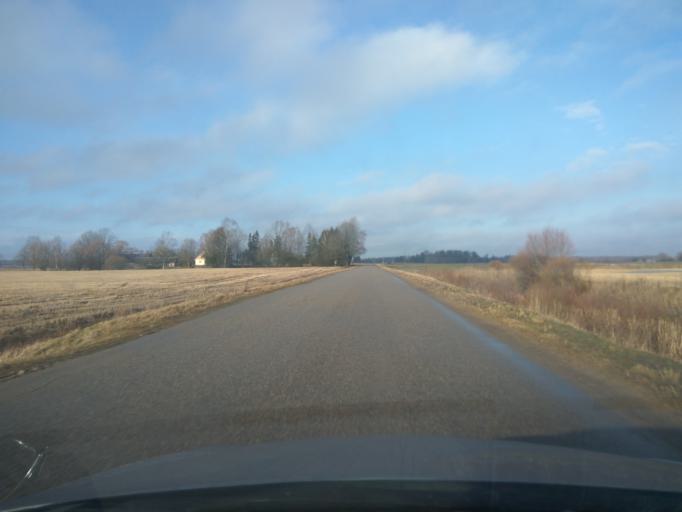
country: LV
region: Saldus Rajons
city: Saldus
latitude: 56.8160
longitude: 22.3794
